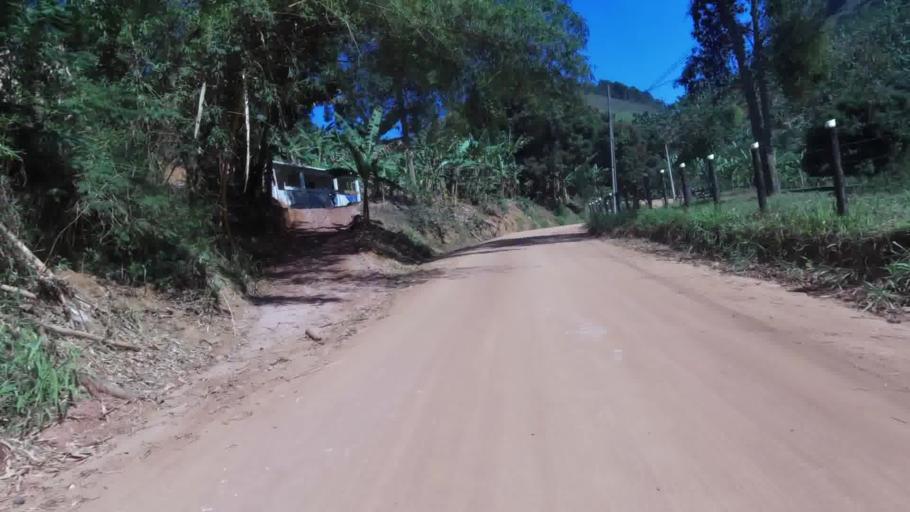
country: BR
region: Espirito Santo
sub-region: Alfredo Chaves
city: Alfredo Chaves
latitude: -20.6453
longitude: -40.7975
